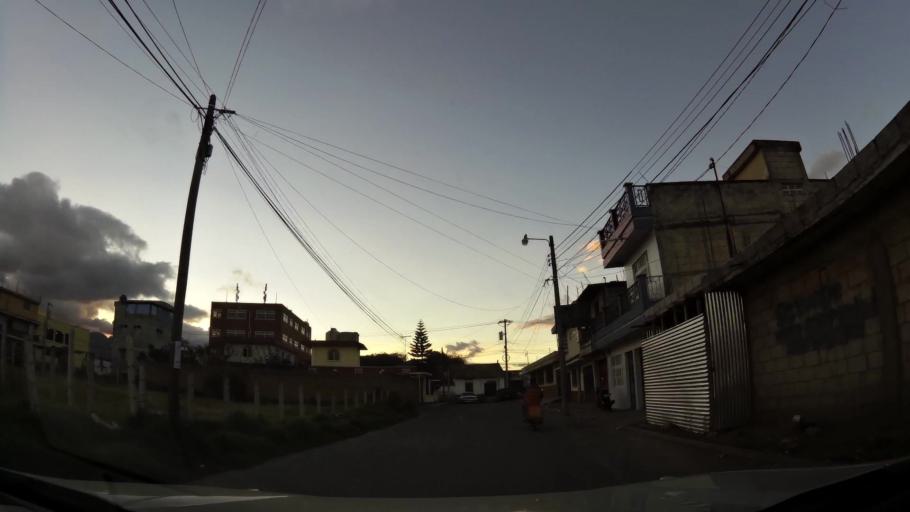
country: GT
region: Quetzaltenango
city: Quetzaltenango
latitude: 14.8541
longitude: -91.5117
